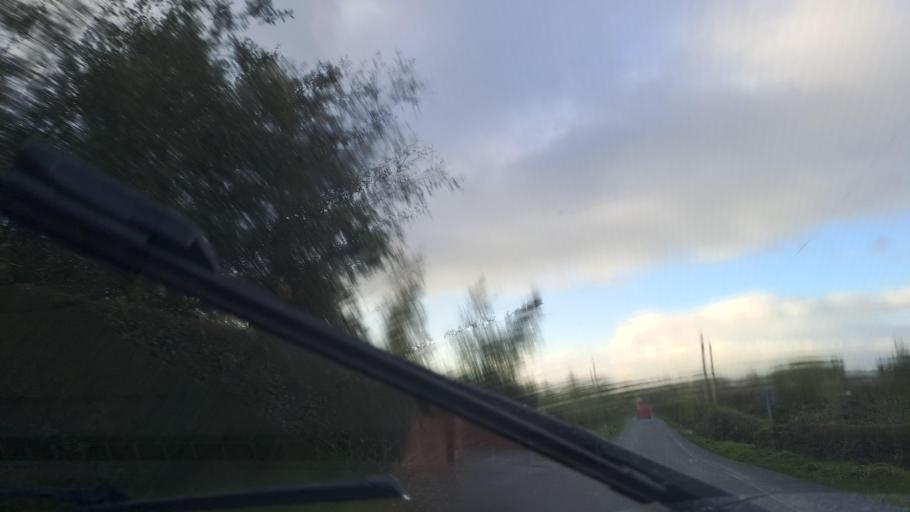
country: IE
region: Ulster
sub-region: County Monaghan
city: Carrickmacross
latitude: 54.0341
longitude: -6.8134
